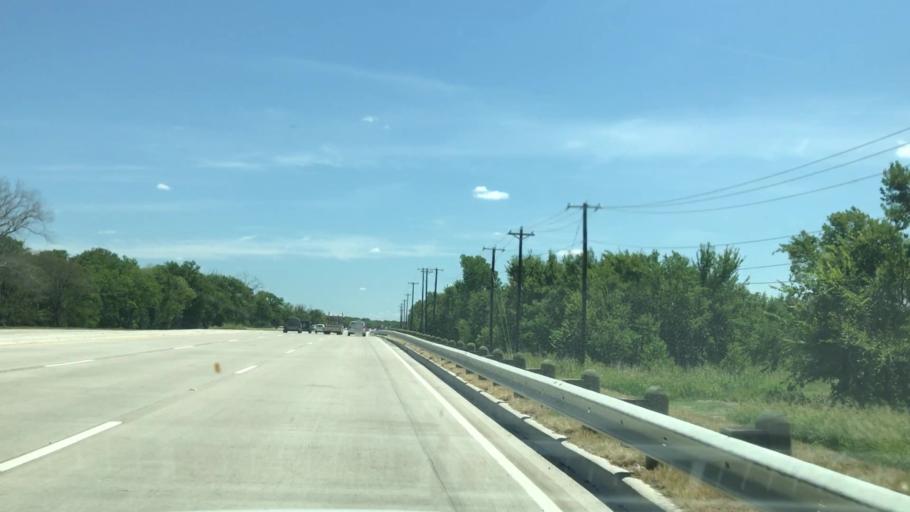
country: US
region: Texas
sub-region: Collin County
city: Lavon
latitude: 33.0254
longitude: -96.4830
